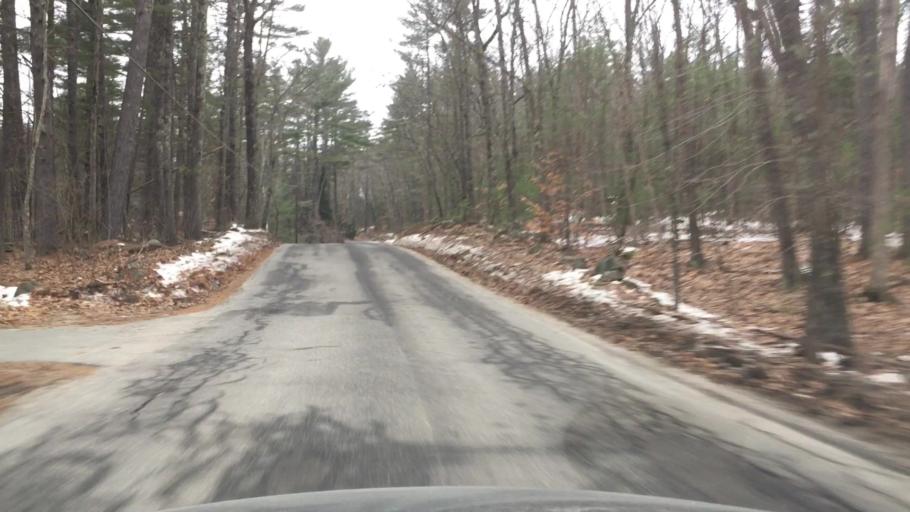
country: US
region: New Hampshire
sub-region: Hillsborough County
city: New Boston
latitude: 43.0083
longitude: -71.6696
